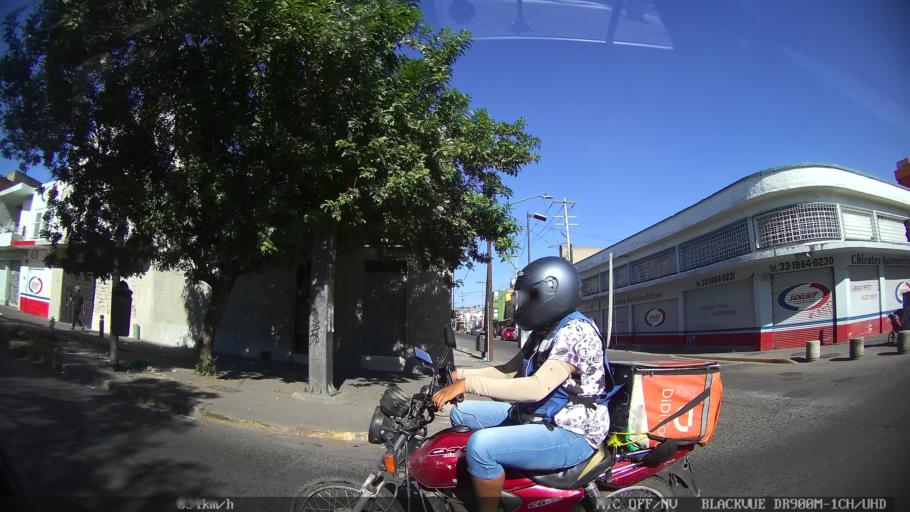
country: MX
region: Jalisco
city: Guadalajara
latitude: 20.6645
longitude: -103.3474
